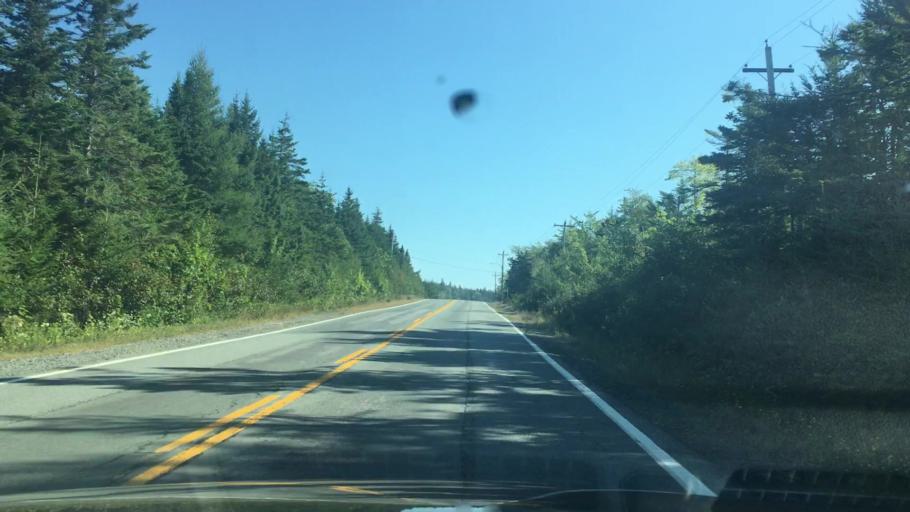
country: CA
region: Nova Scotia
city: Cole Harbour
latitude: 44.7764
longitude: -63.0476
